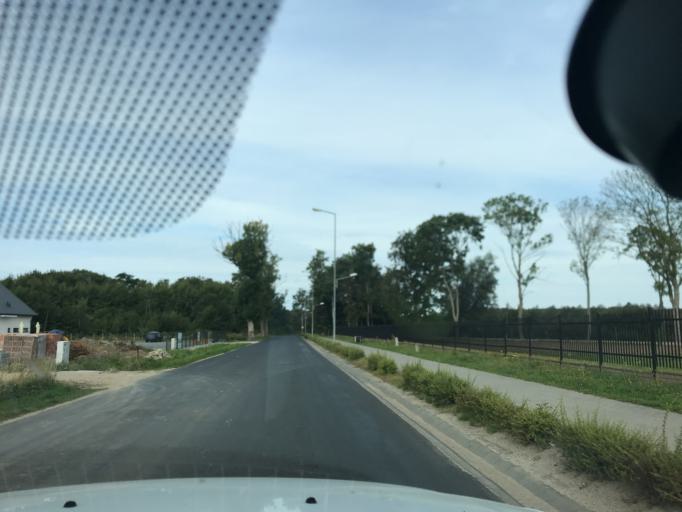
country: PL
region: West Pomeranian Voivodeship
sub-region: Powiat slawienski
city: Darlowo
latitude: 54.5345
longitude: 16.5750
